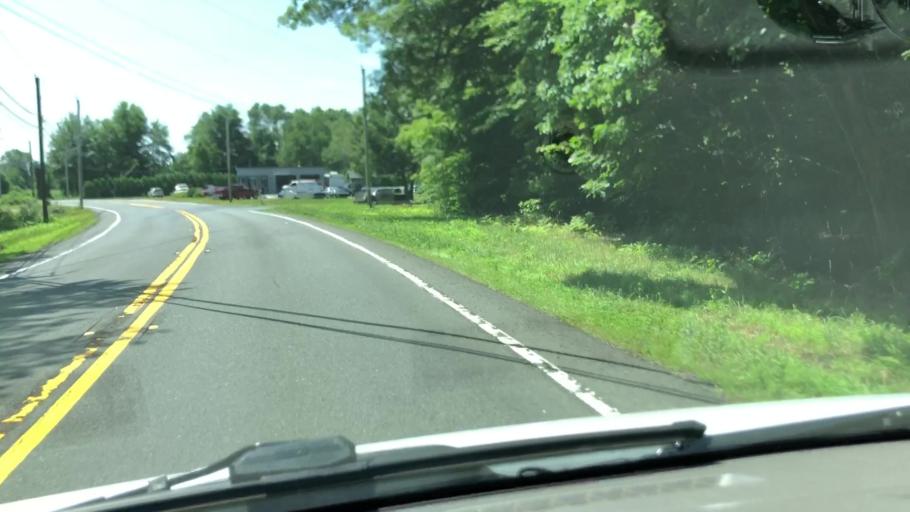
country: US
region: Massachusetts
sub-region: Franklin County
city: Whately
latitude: 42.4520
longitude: -72.6268
